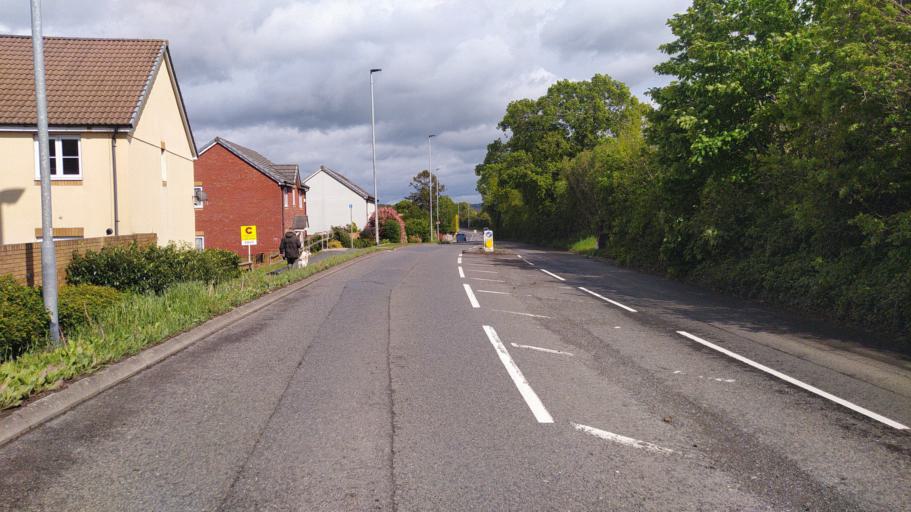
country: GB
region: England
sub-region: Devon
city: Newton Abbot
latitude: 50.5365
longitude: -3.6422
